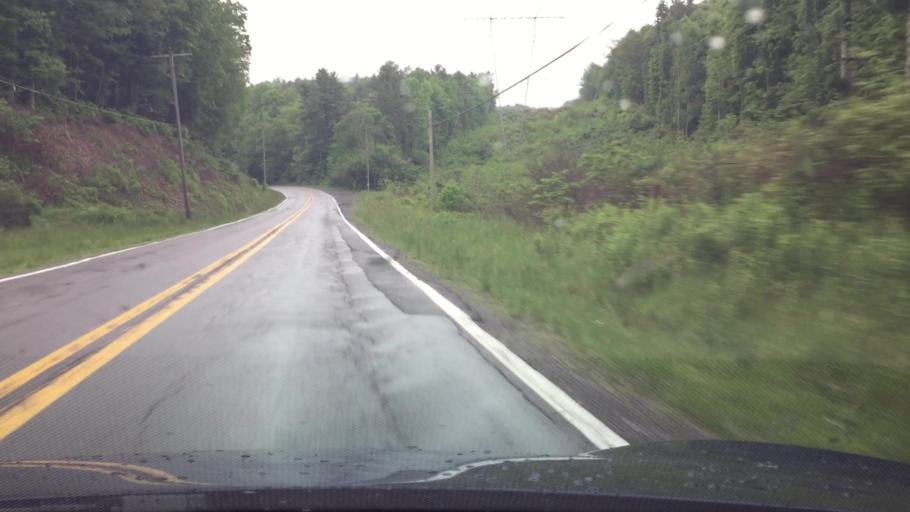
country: US
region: West Virginia
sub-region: Raleigh County
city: Shady Spring
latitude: 37.6883
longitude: -81.0597
